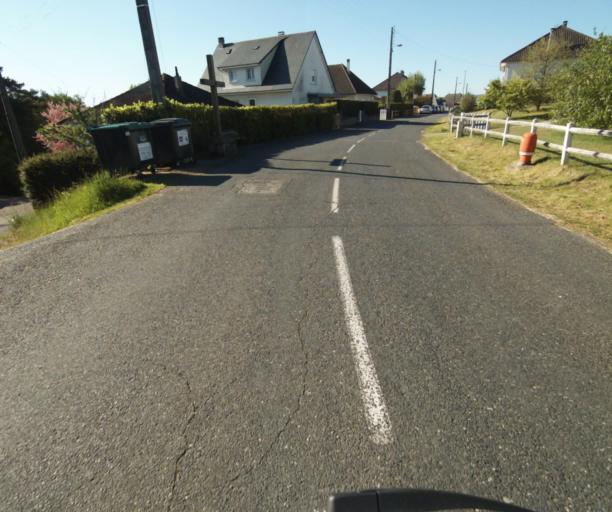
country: FR
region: Limousin
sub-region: Departement de la Correze
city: Tulle
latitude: 45.2689
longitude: 1.7860
